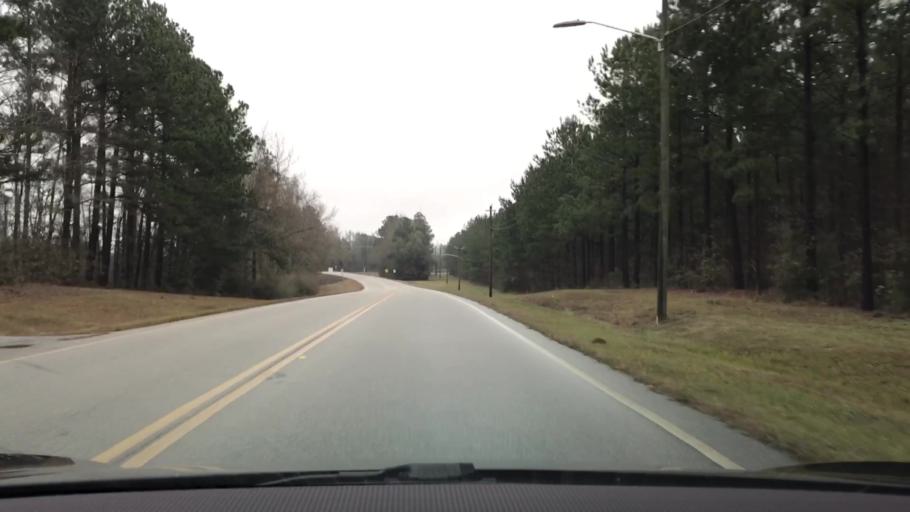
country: US
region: Georgia
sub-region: Jefferson County
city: Wrens
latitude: 33.2209
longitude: -82.4643
